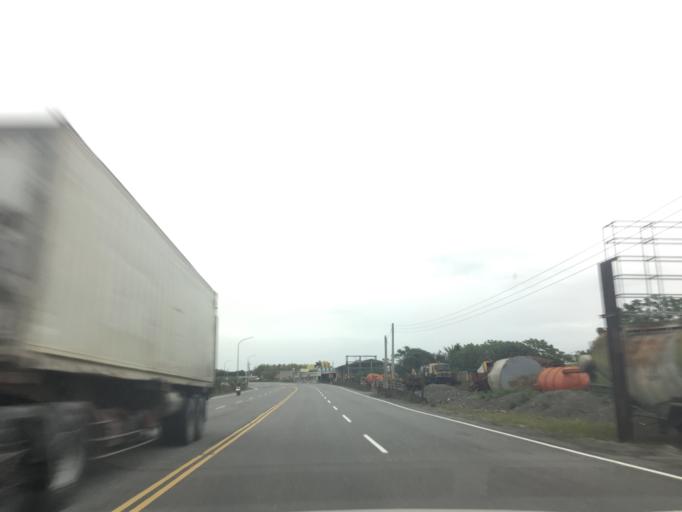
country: TW
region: Taiwan
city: Taitung City
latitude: 22.7253
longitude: 121.0557
